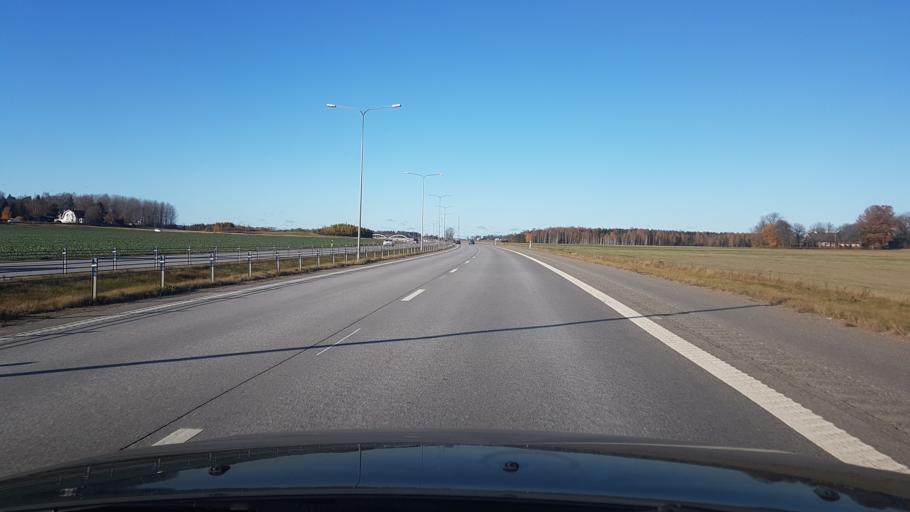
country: SE
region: Uppsala
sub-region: Uppsala Kommun
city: Saevja
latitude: 59.8604
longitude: 17.7258
